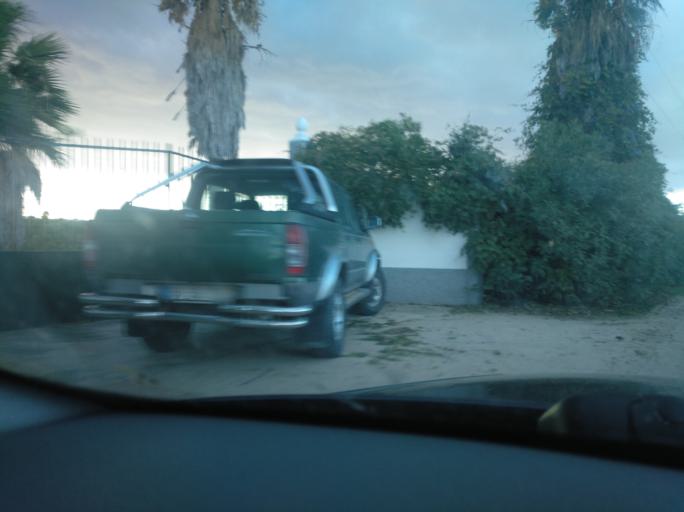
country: PT
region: Portalegre
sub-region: Campo Maior
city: Campo Maior
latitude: 39.0123
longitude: -7.0516
